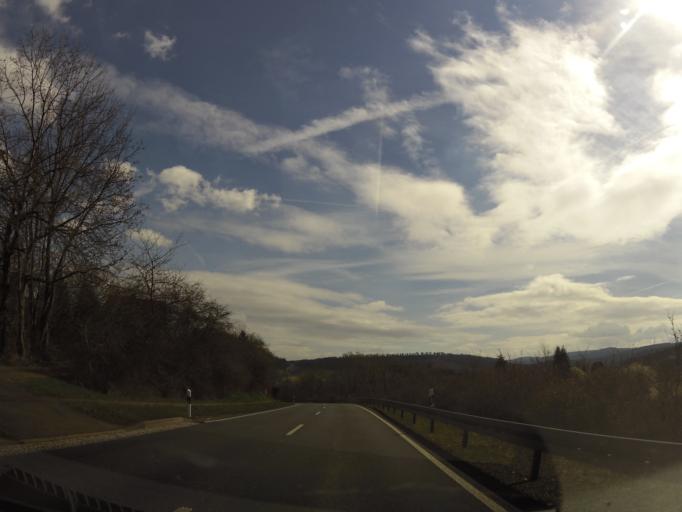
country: DE
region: Thuringia
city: Grafenroda
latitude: 50.7510
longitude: 10.7963
